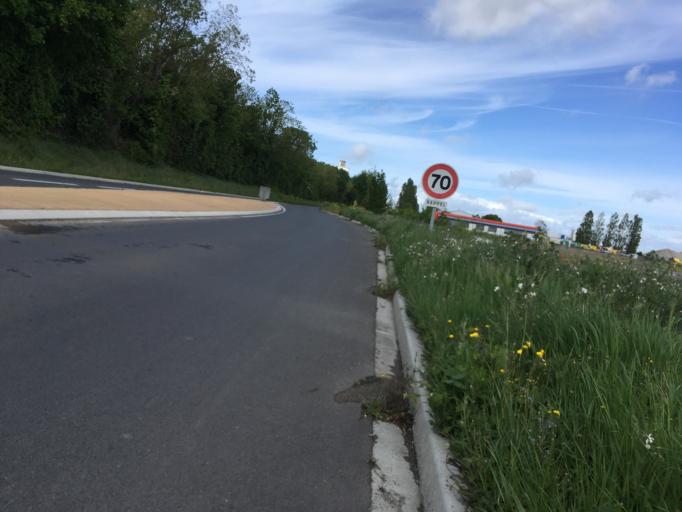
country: FR
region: Poitou-Charentes
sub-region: Departement de la Charente-Maritime
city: Dompierre-sur-Mer
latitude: 46.1715
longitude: -1.0721
